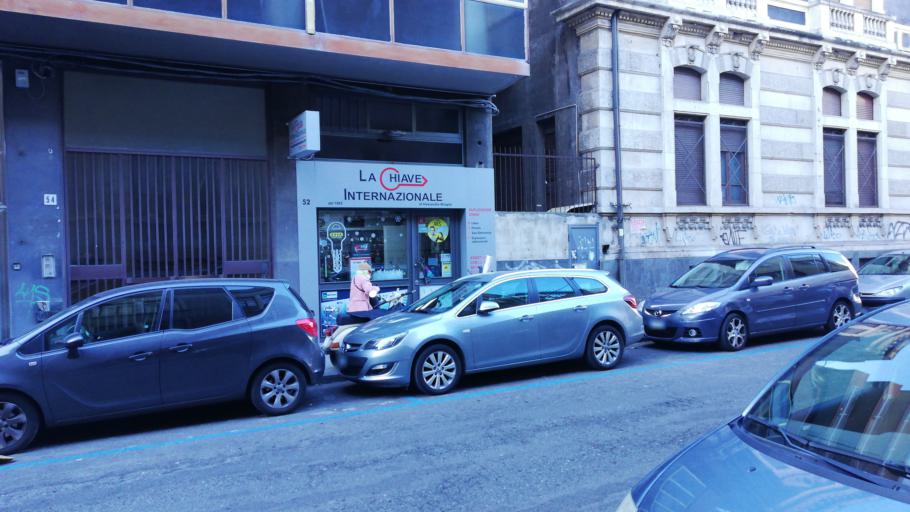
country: IT
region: Sicily
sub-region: Catania
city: Canalicchio
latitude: 37.5175
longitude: 15.0978
